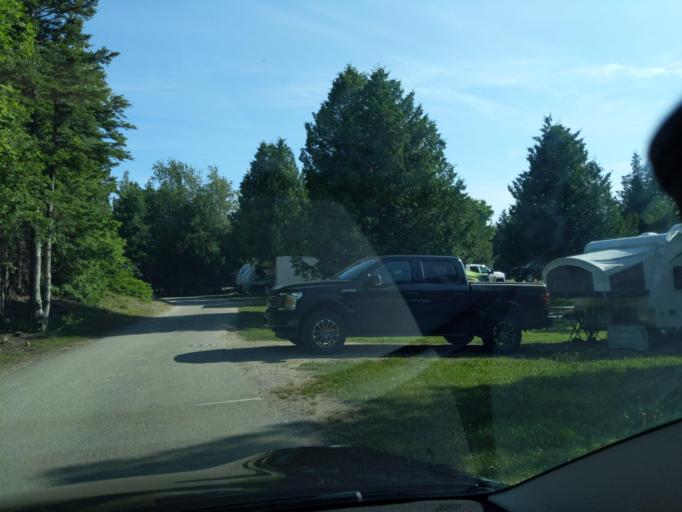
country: US
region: Michigan
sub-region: Mackinac County
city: Saint Ignace
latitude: 45.8537
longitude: -84.7226
